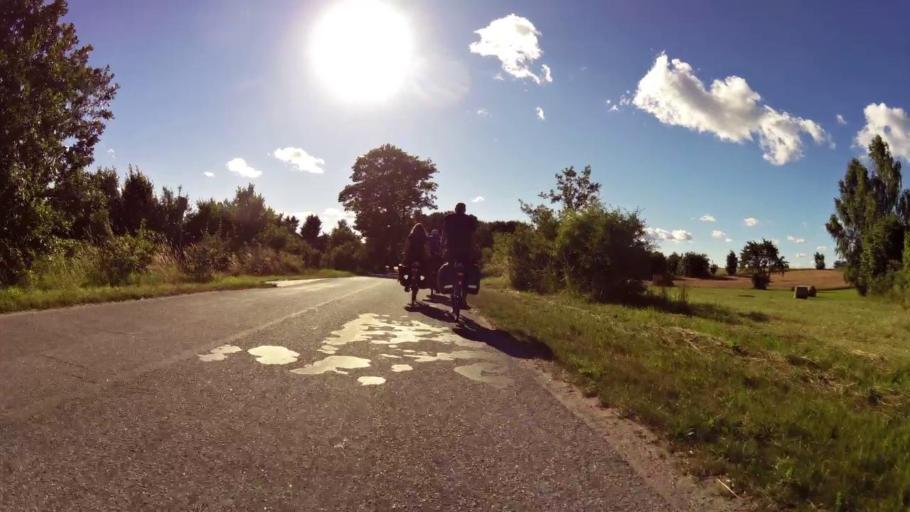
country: PL
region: West Pomeranian Voivodeship
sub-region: Powiat swidwinski
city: Swidwin
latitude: 53.7751
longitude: 15.7492
